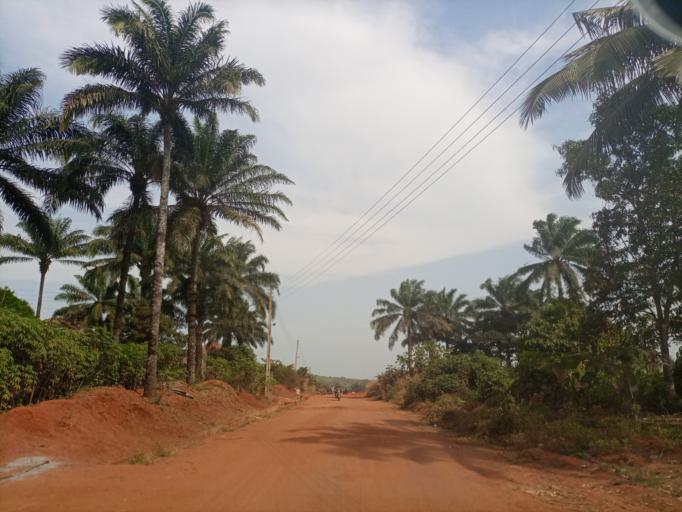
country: NG
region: Enugu
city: Opi
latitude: 6.8221
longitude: 7.4755
